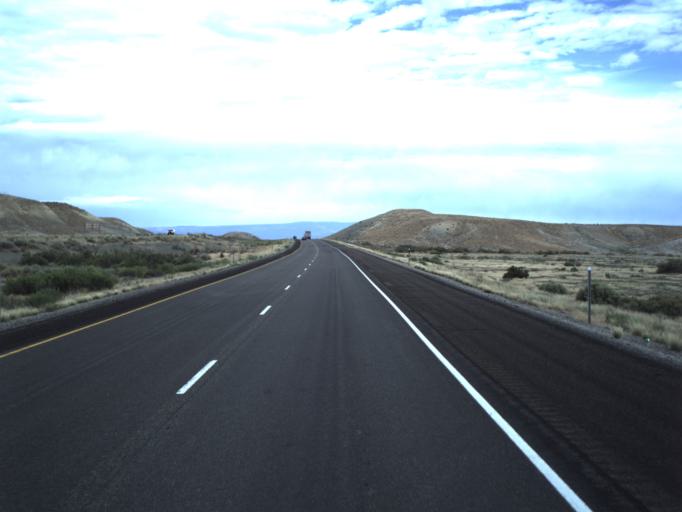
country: US
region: Utah
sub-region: Grand County
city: Moab
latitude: 38.9430
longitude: -109.6378
